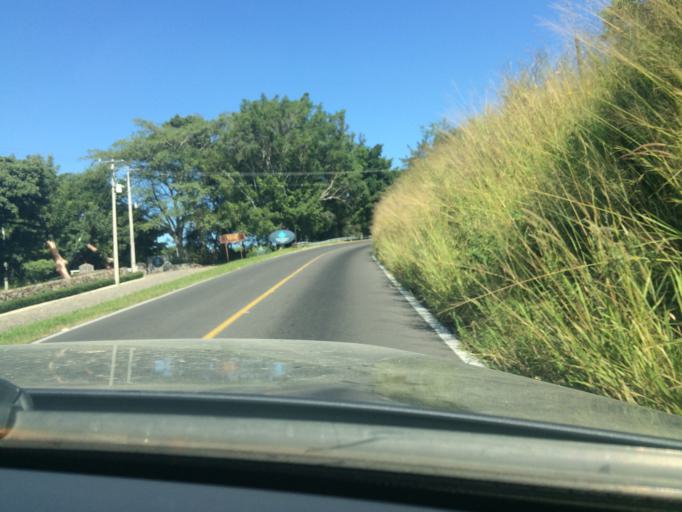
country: MX
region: Colima
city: Suchitlan
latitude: 19.3708
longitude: -103.7222
